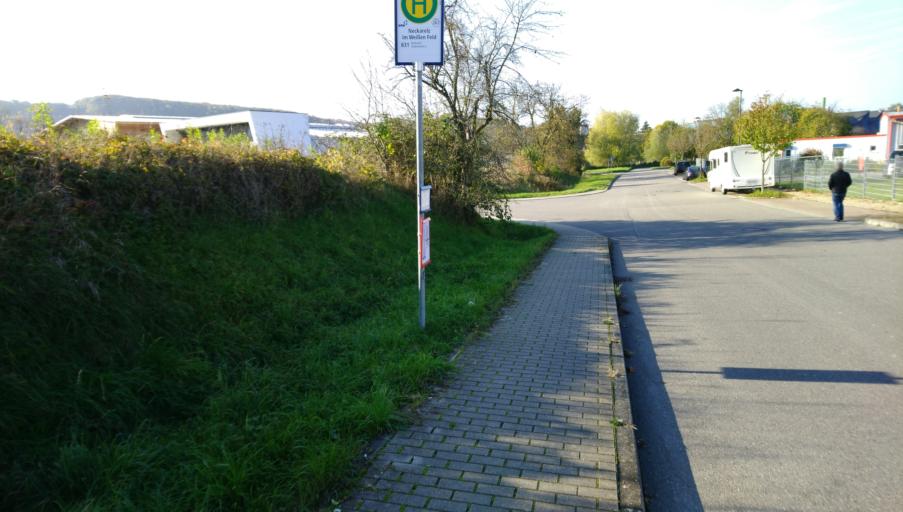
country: DE
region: Baden-Wuerttemberg
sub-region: Karlsruhe Region
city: Obrigheim
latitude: 49.3370
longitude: 9.1121
